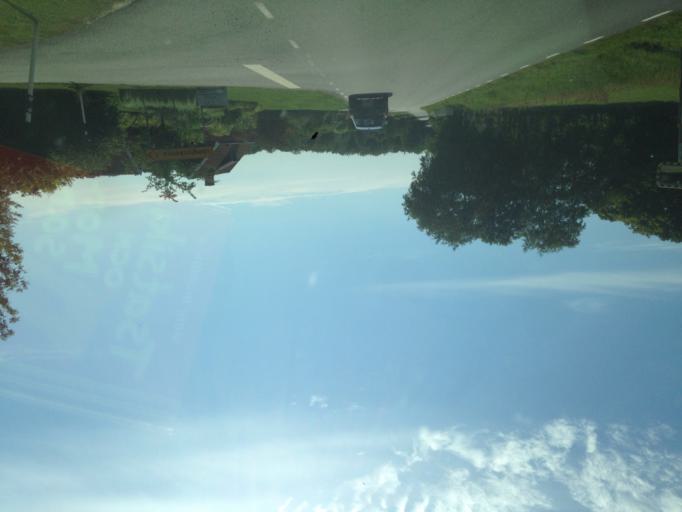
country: SE
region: Skane
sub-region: Simrishamns Kommun
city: Kivik
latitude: 55.6350
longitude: 14.1565
